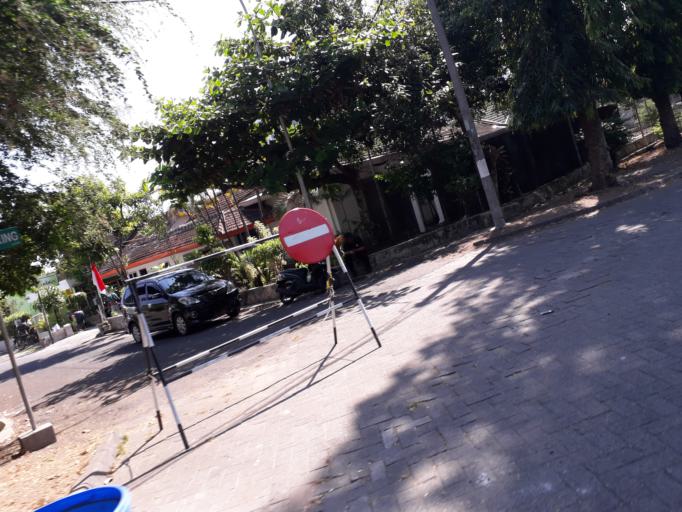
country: ID
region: Daerah Istimewa Yogyakarta
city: Yogyakarta
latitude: -7.7711
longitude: 110.3739
